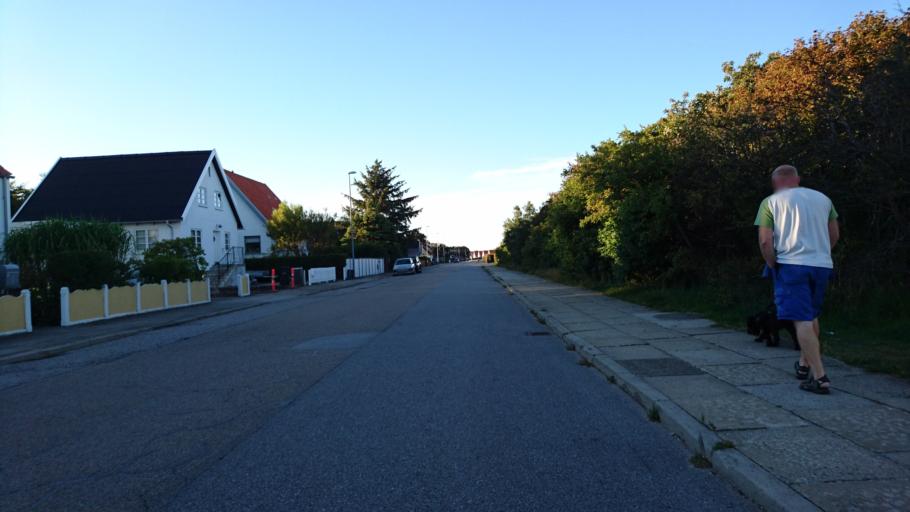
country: DK
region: North Denmark
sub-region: Frederikshavn Kommune
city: Skagen
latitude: 57.7283
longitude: 10.5829
